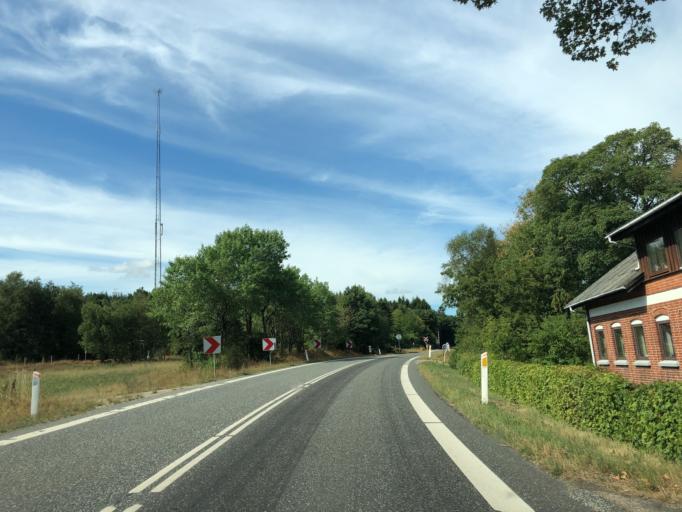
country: DK
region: Central Jutland
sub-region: Silkeborg Kommune
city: Silkeborg
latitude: 56.1388
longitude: 9.4108
